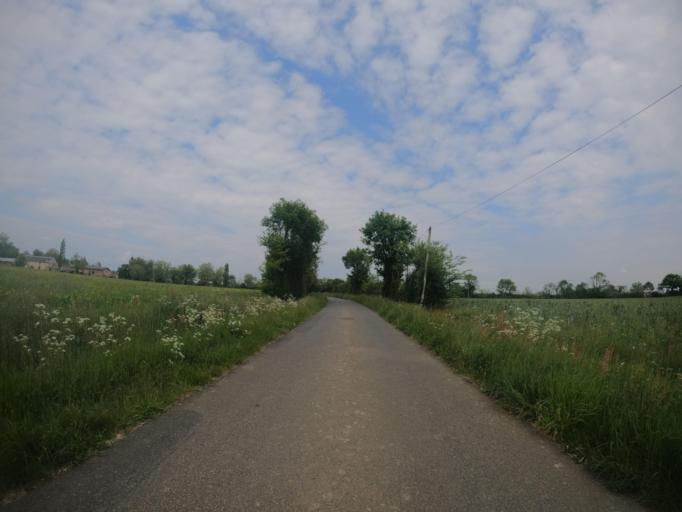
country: FR
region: Poitou-Charentes
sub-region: Departement des Deux-Sevres
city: Saint-Varent
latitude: 46.8765
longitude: -0.2823
